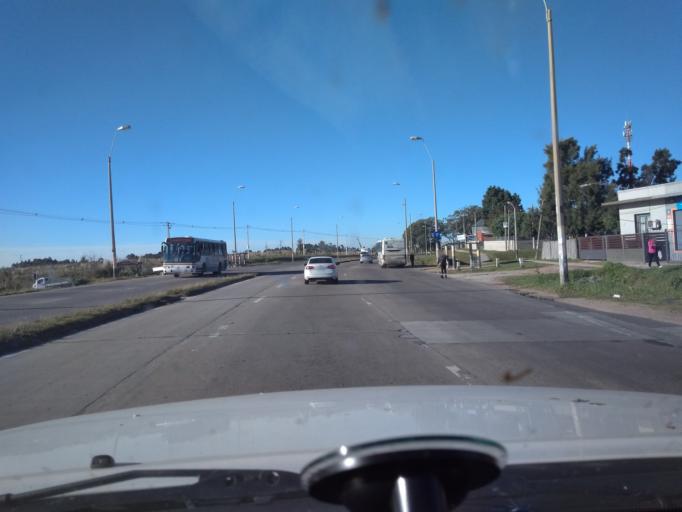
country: UY
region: Canelones
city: Colonia Nicolich
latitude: -34.7765
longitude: -56.0531
